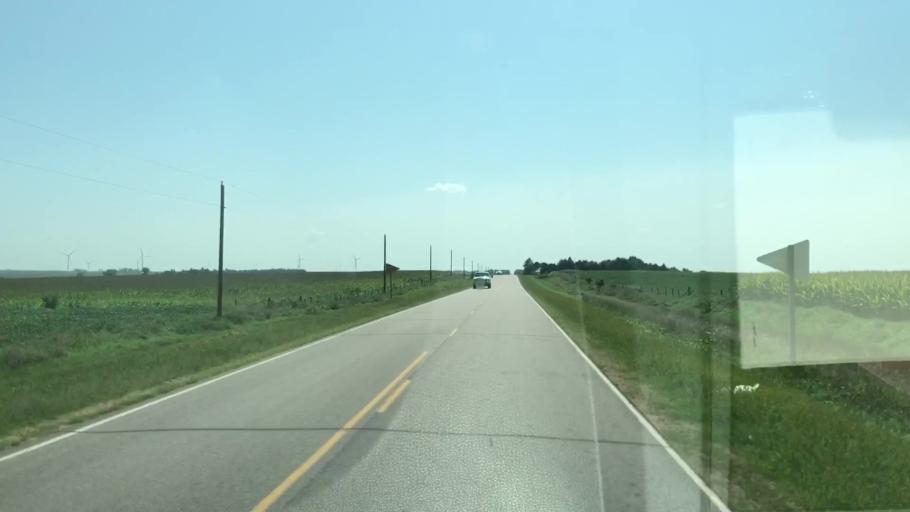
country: US
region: Iowa
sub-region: O'Brien County
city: Sanborn
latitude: 43.2557
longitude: -95.7235
